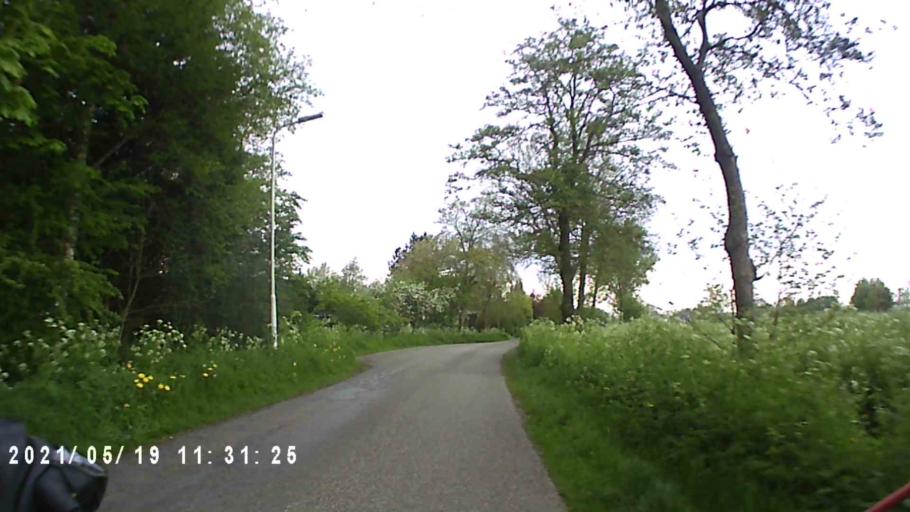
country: NL
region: Friesland
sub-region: Gemeente Kollumerland en Nieuwkruisland
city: Kollum
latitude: 53.2741
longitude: 6.1746
